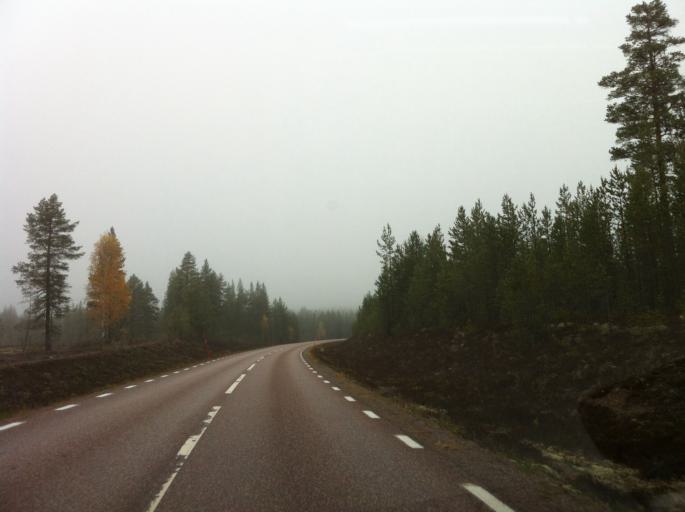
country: NO
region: Hedmark
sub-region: Trysil
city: Innbygda
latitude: 61.7469
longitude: 12.9704
